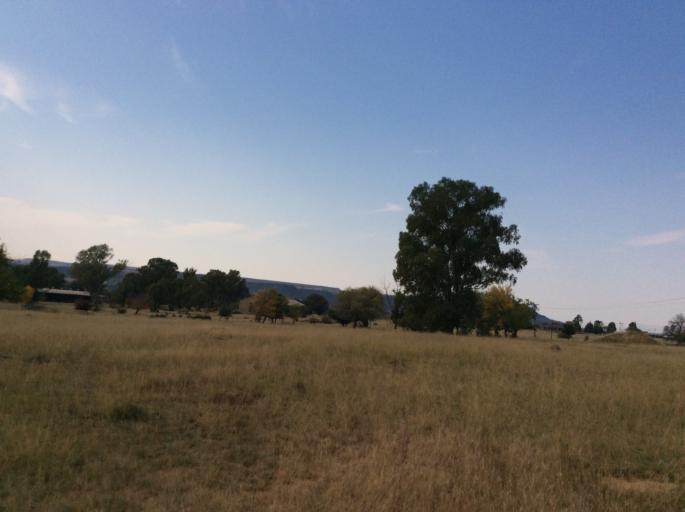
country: LS
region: Mafeteng
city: Mafeteng
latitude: -29.7330
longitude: 27.0241
